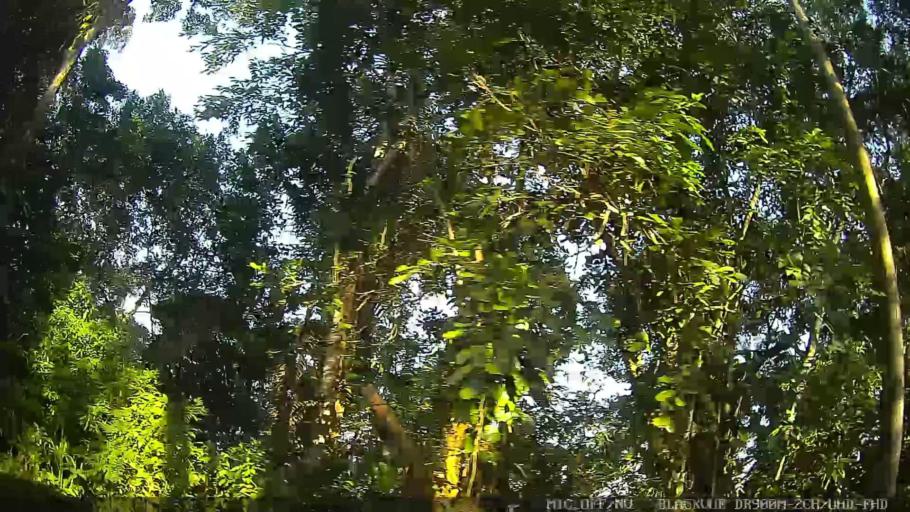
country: BR
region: Sao Paulo
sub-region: Guaruja
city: Guaruja
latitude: -23.9815
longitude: -46.2536
